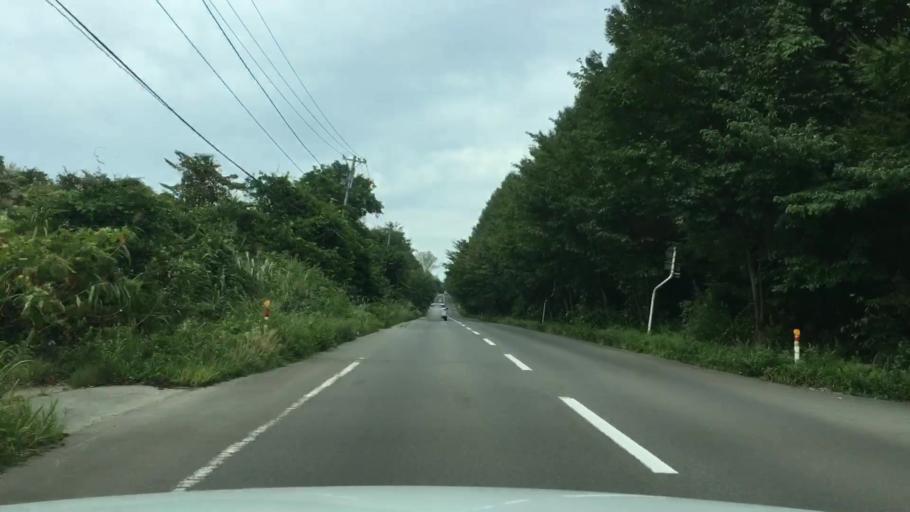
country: JP
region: Aomori
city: Shimokizukuri
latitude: 40.7142
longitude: 140.3205
